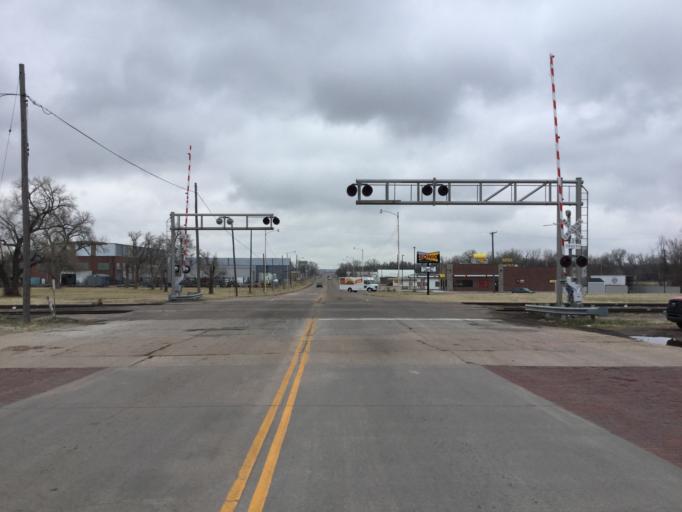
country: US
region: Kansas
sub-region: Barton County
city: Hoisington
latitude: 38.5116
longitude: -98.7774
